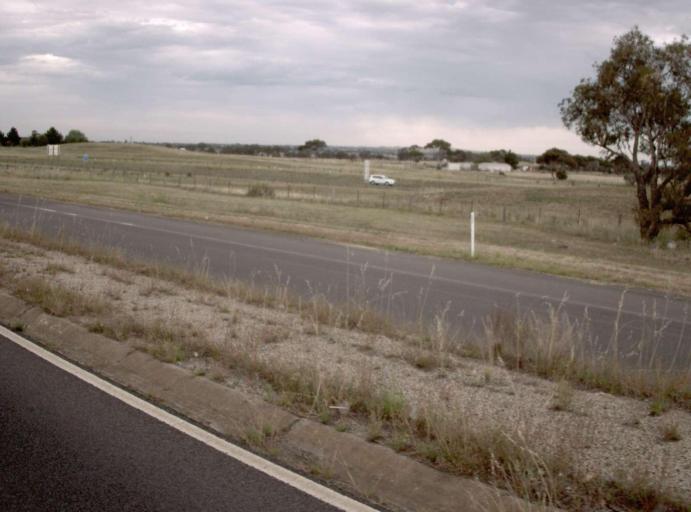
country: AU
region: Victoria
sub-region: Melton
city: Brookfield
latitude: -37.6869
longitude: 144.5249
